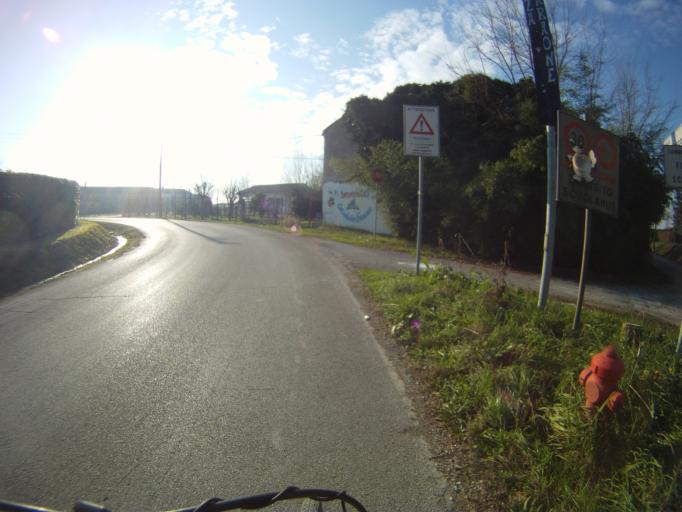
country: IT
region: Veneto
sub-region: Provincia di Padova
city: Brugine
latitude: 45.2916
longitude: 11.9962
